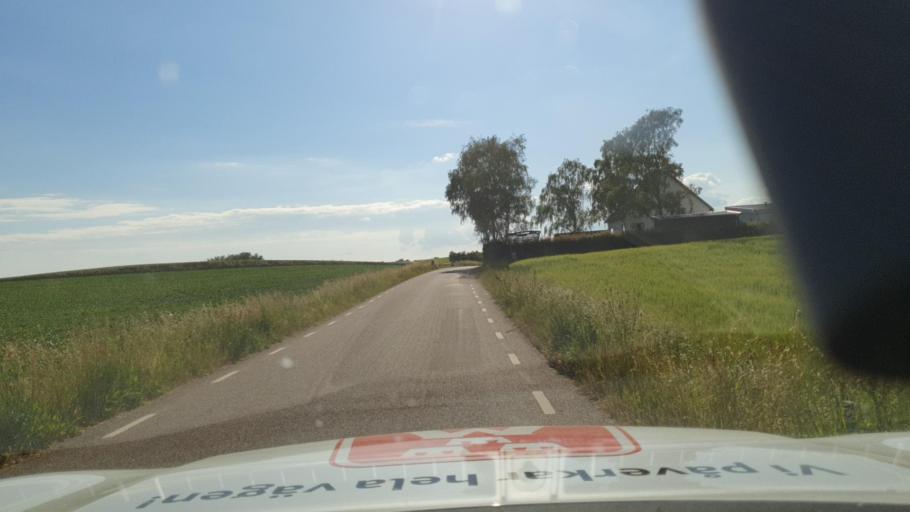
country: SE
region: Skane
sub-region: Ystads Kommun
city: Ystad
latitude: 55.4465
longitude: 13.7061
